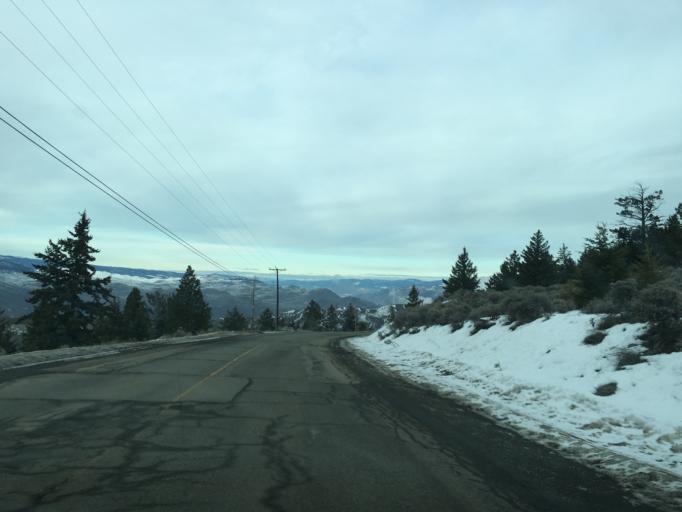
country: CA
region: British Columbia
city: Kamloops
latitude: 50.6539
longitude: -120.4507
